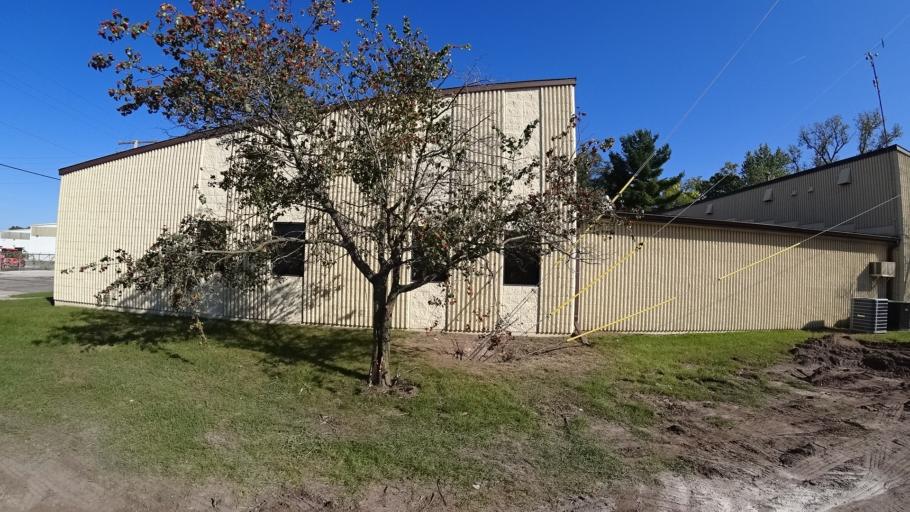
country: US
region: Indiana
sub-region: LaPorte County
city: Michigan City
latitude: 41.7024
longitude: -86.9082
